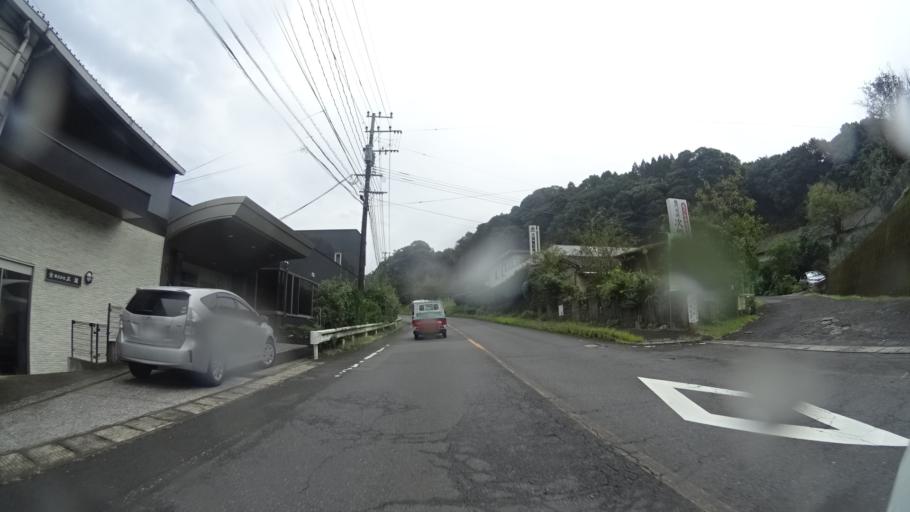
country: JP
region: Kagoshima
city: Kajiki
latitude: 31.7661
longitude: 130.6707
